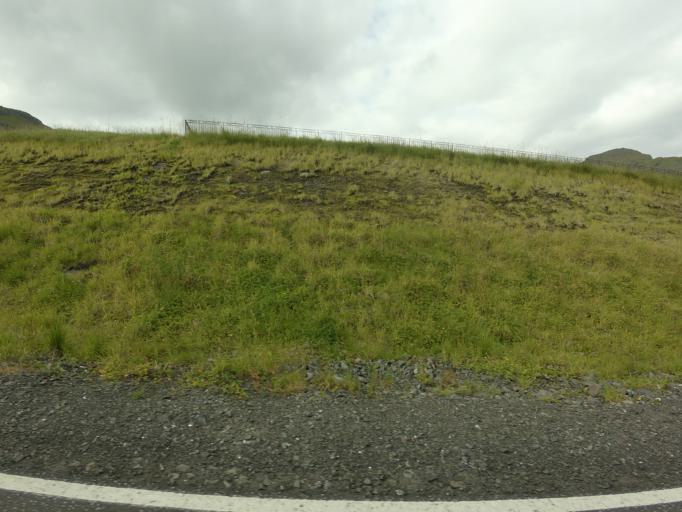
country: FO
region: Eysturoy
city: Eystur
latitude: 62.2104
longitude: -6.6986
